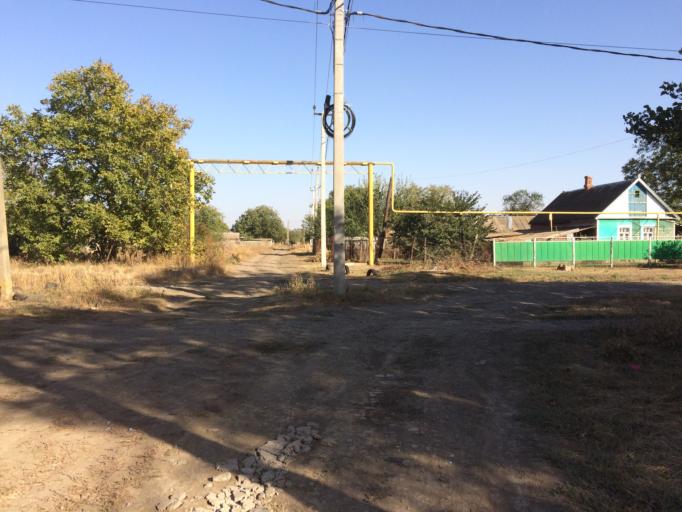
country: RU
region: Rostov
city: Tselina
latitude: 46.5217
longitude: 41.1834
